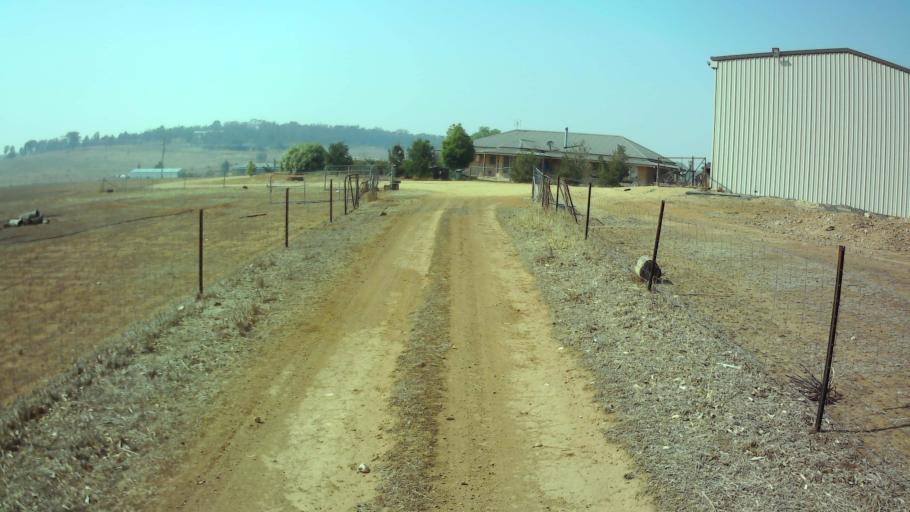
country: AU
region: New South Wales
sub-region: Weddin
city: Grenfell
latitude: -33.8969
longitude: 148.1795
